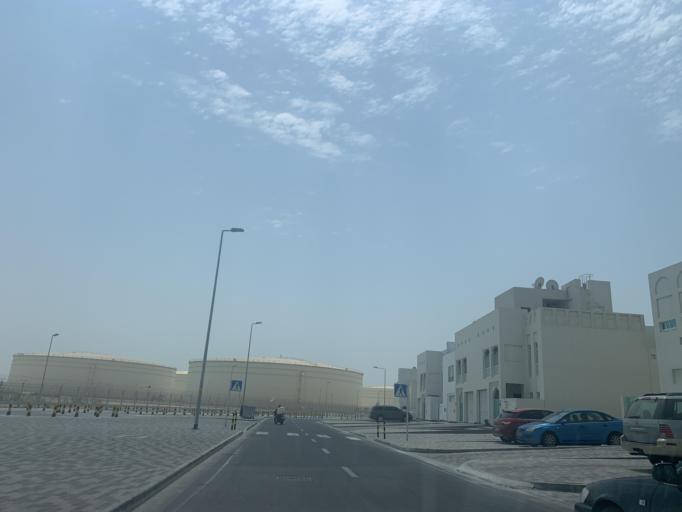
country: BH
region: Muharraq
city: Al Hadd
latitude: 26.2318
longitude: 50.6663
